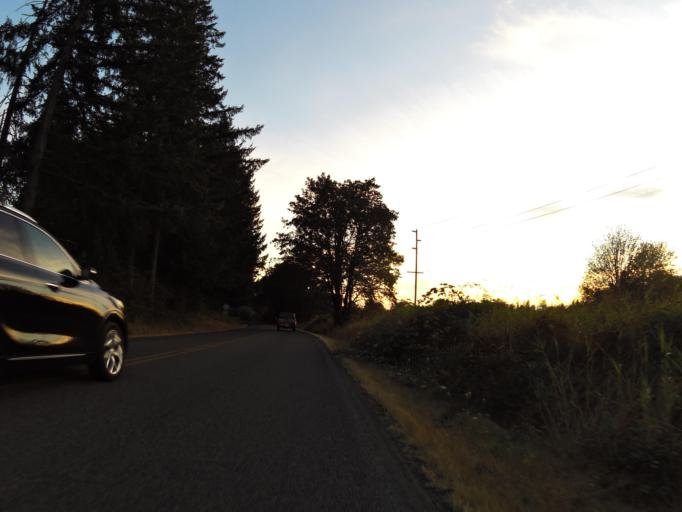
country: US
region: Washington
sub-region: Thurston County
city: Tenino
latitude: 46.8501
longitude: -122.8581
